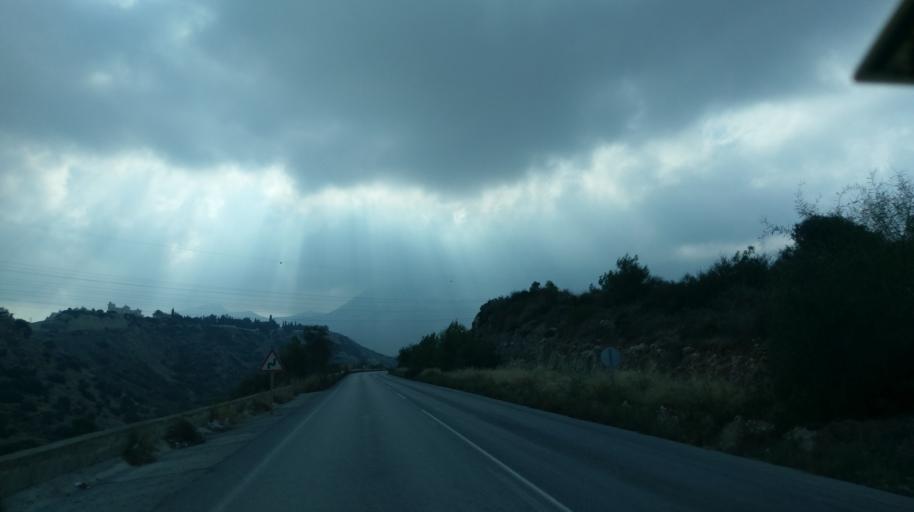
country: CY
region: Keryneia
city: Kyrenia
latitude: 35.3172
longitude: 33.4223
